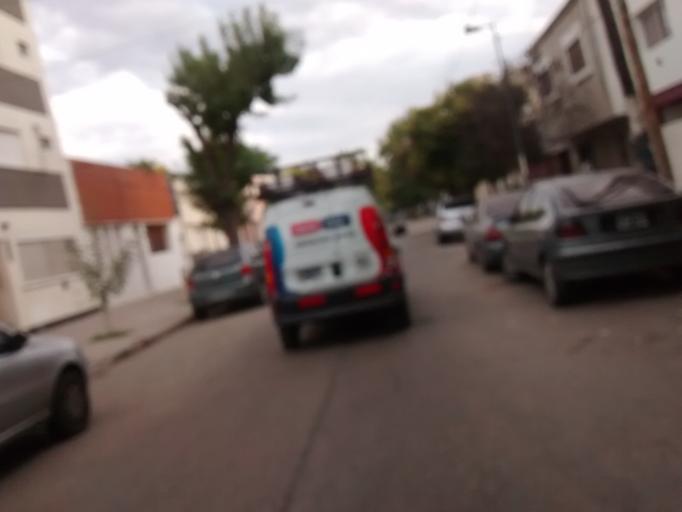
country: AR
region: Buenos Aires
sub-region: Partido de La Plata
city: La Plata
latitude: -34.9189
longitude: -57.9281
